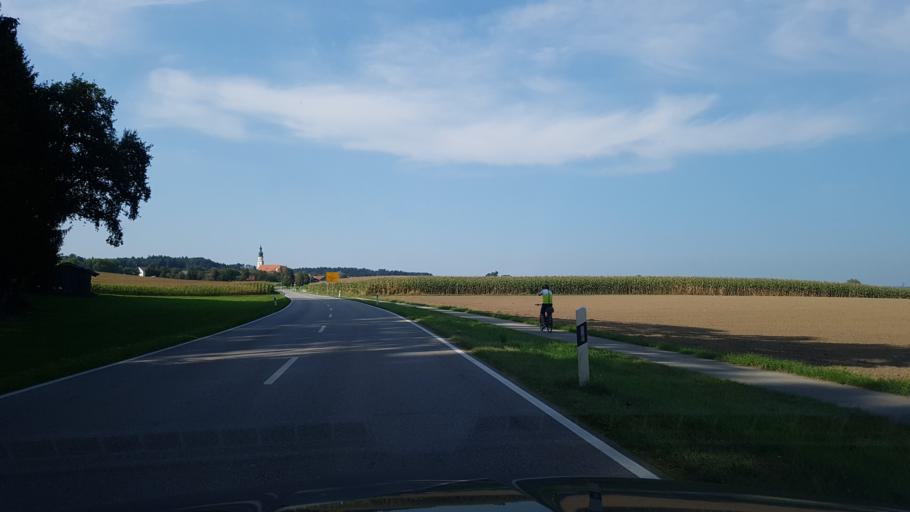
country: DE
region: Bavaria
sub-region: Upper Bavaria
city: Ainring
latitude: 47.8607
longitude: 12.9354
